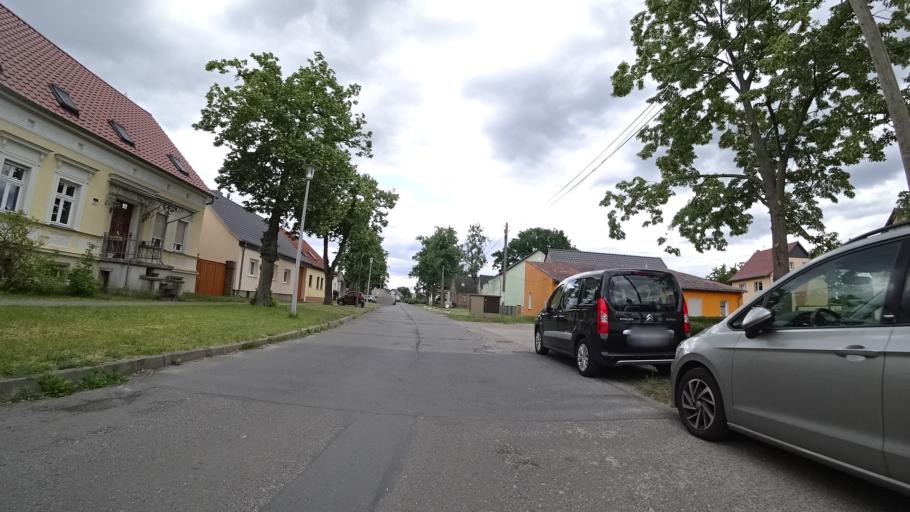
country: DE
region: Brandenburg
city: Trebbin
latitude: 52.1934
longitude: 13.2437
